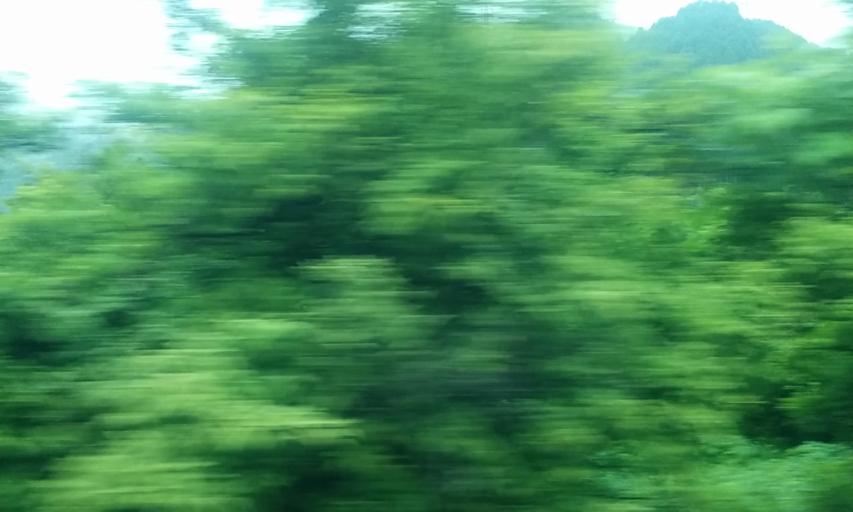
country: JP
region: Tokyo
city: Ome
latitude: 35.8065
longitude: 139.1880
